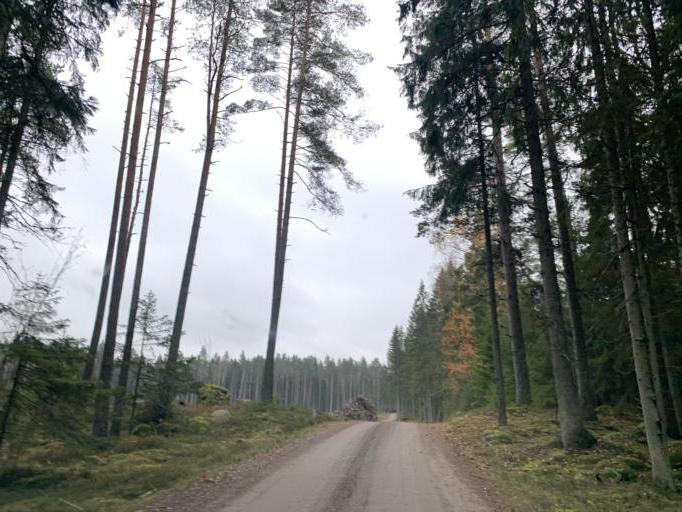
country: SE
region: Vaestmanland
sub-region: Kopings Kommun
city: Koping
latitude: 59.6291
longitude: 16.0649
